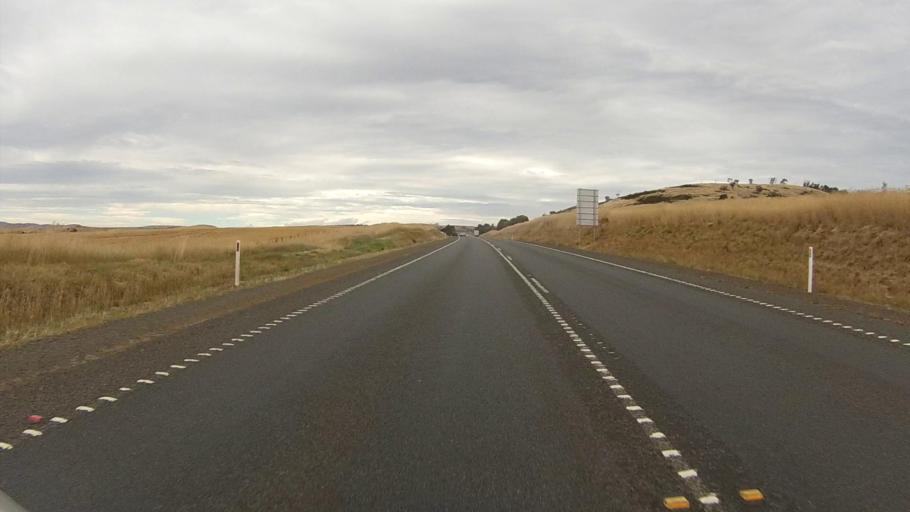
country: AU
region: Tasmania
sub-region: Brighton
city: Bridgewater
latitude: -42.3825
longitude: 147.3173
